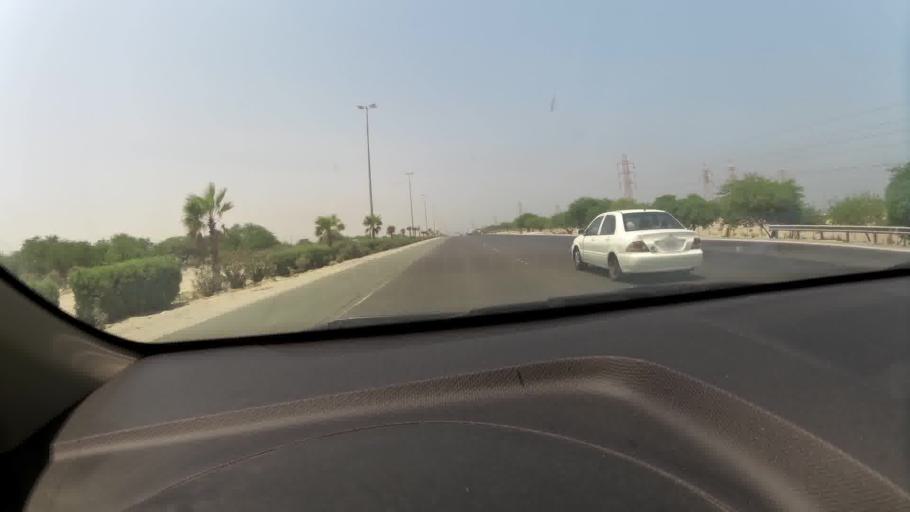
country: KW
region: Al Ahmadi
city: Al Fahahil
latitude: 28.8723
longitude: 48.2336
